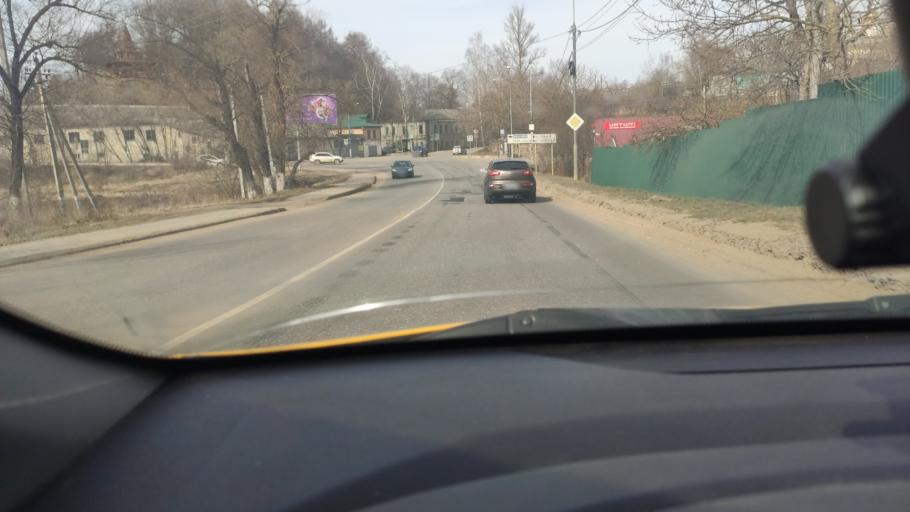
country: RU
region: Moskovskaya
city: Ruza
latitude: 55.6967
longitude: 36.1955
